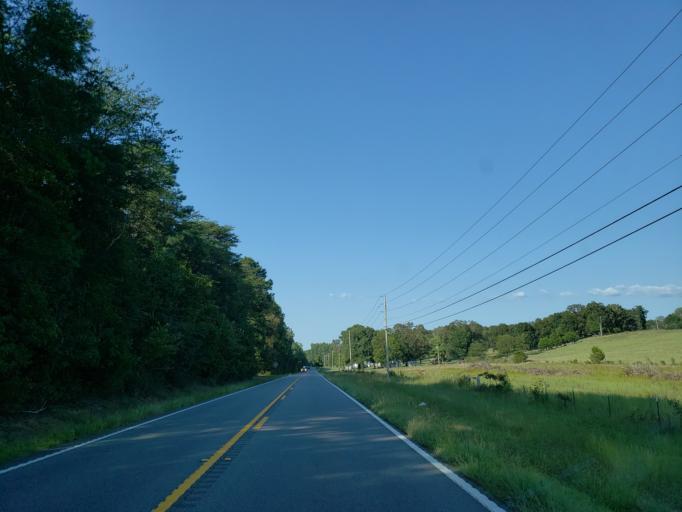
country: US
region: Tennessee
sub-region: Bradley County
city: Wildwood Lake
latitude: 34.9490
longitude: -84.7772
